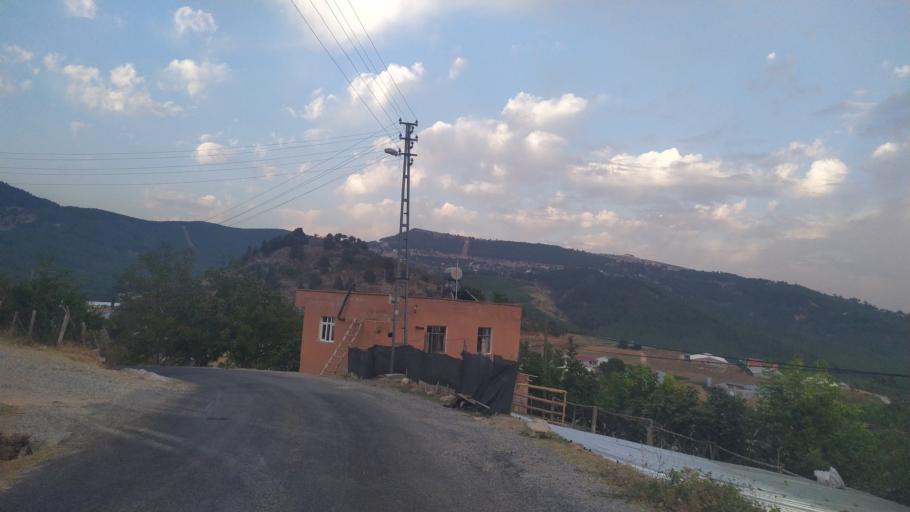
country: TR
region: Mersin
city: Camliyayla
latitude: 37.2311
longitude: 34.7149
